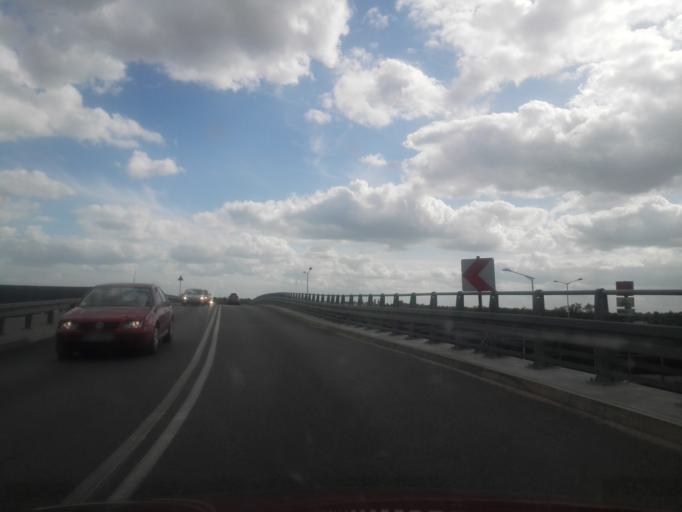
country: PL
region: Masovian Voivodeship
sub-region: Powiat wolominski
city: Marki
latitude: 52.3081
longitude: 21.0786
